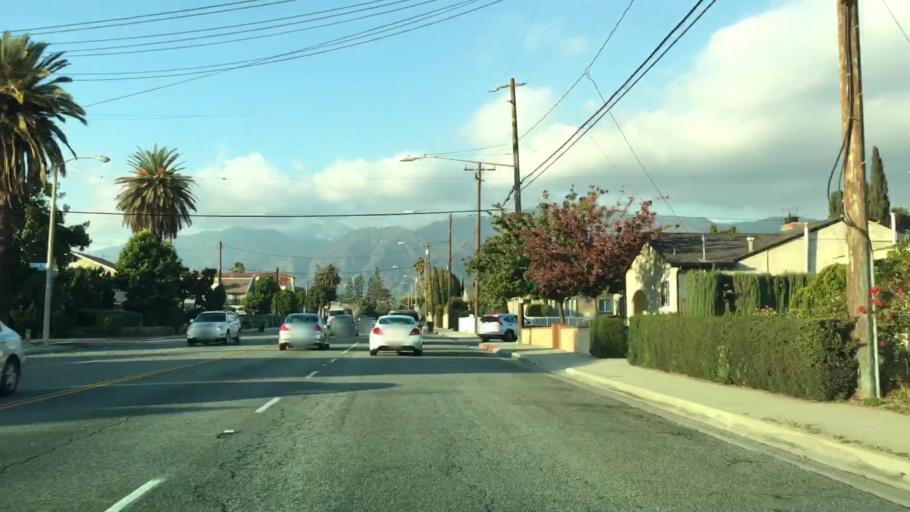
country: US
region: California
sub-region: Los Angeles County
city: Temple City
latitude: 34.1223
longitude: -118.0640
